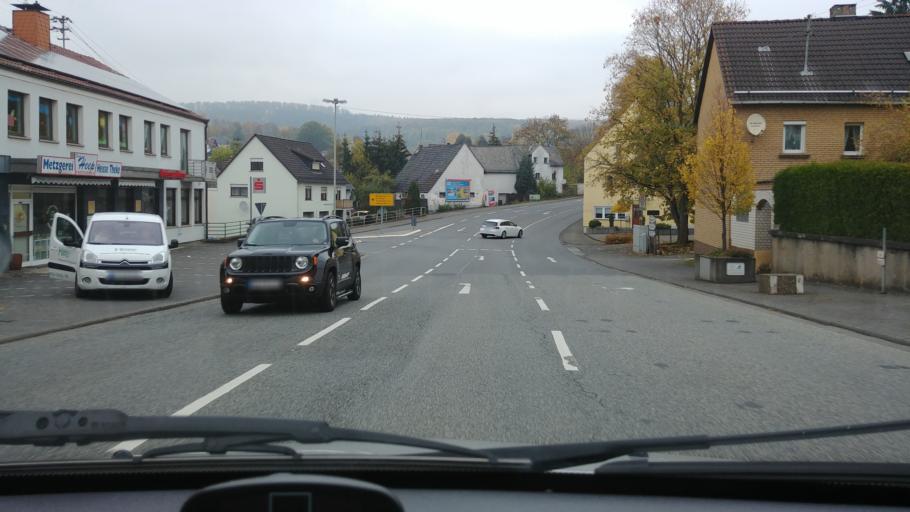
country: DE
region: Rheinland-Pfalz
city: Irmtraut
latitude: 50.5389
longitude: 8.0484
